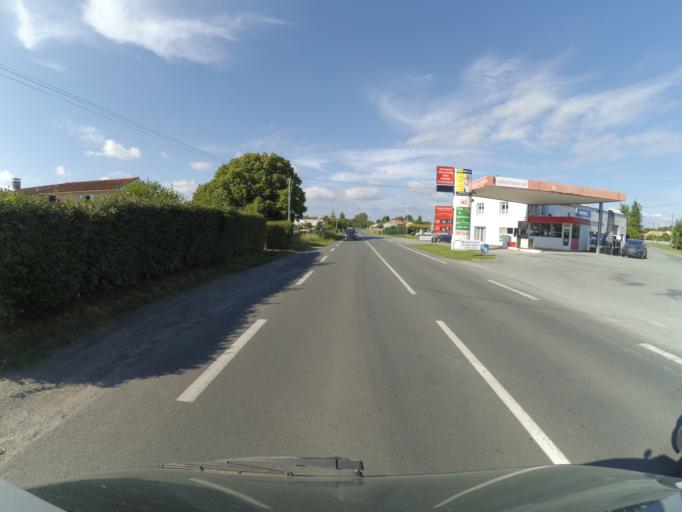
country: FR
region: Poitou-Charentes
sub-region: Departement de la Charente-Maritime
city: Le Gua
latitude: 45.7252
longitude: -0.9636
